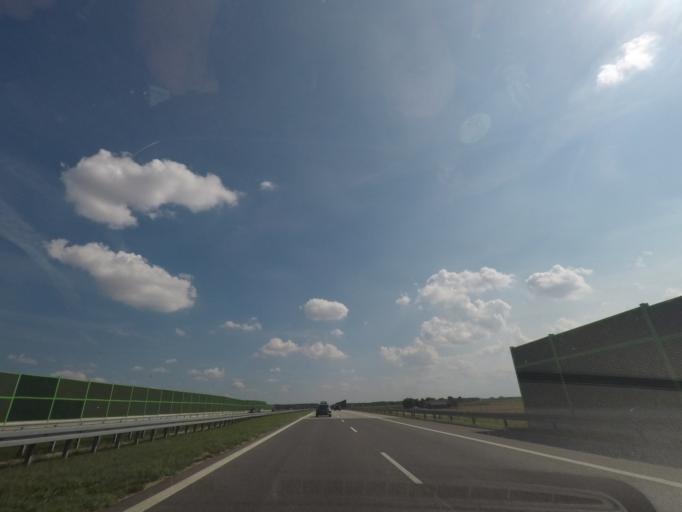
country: PL
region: Lodz Voivodeship
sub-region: Powiat lodzki wschodni
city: Tuszyn
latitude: 51.5795
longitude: 19.5936
